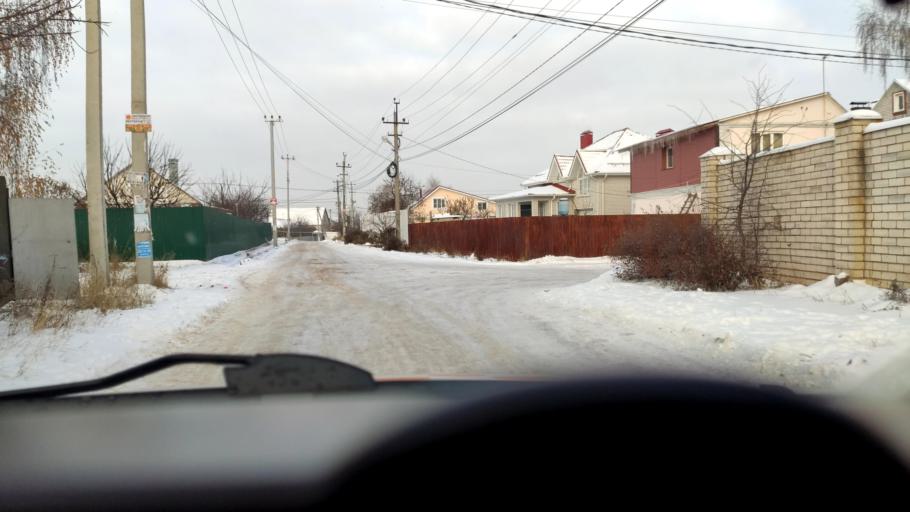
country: RU
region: Voronezj
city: Podgornoye
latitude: 51.7277
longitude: 39.1597
